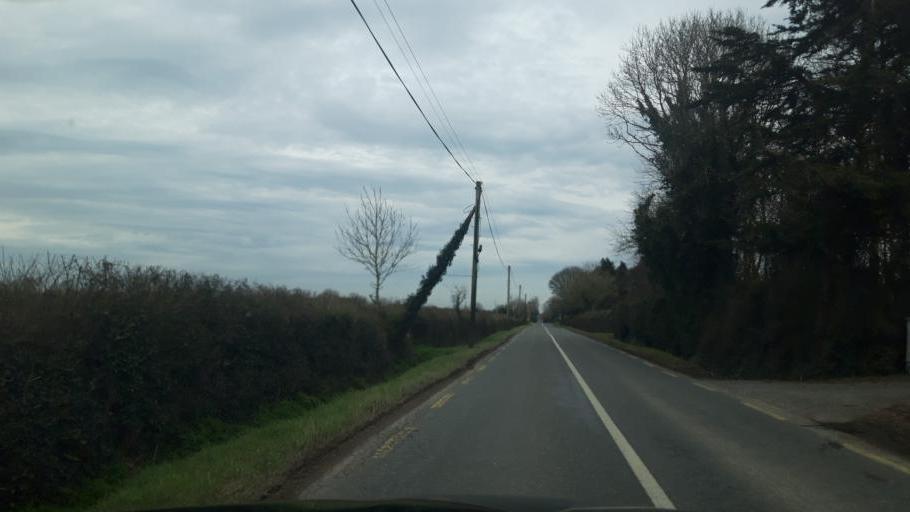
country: IE
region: Leinster
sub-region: Kildare
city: Prosperous
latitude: 53.3054
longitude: -6.7268
